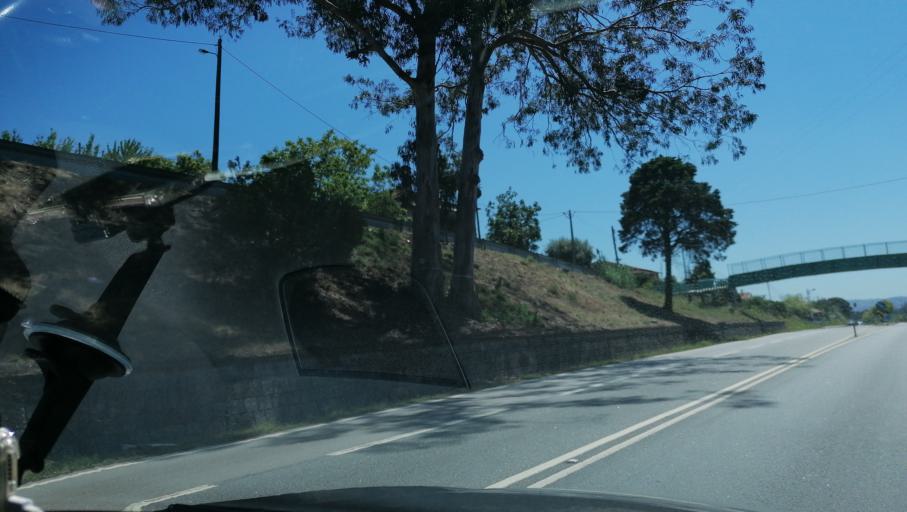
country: PT
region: Aveiro
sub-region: Mealhada
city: Pampilhosa do Botao
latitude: 40.2904
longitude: -8.4461
